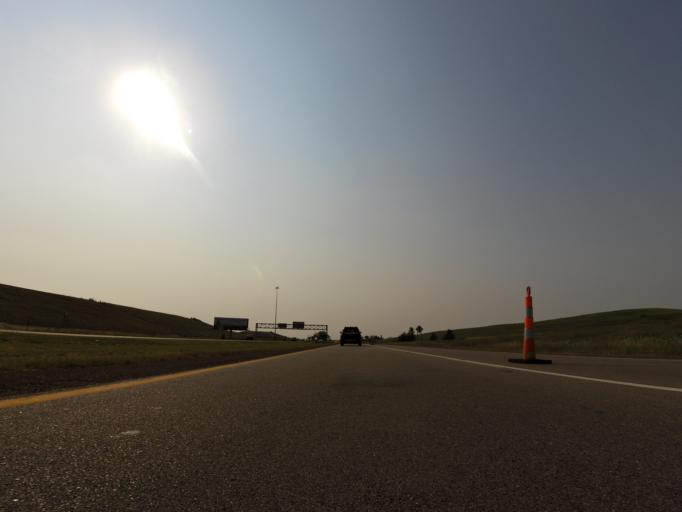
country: US
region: Kansas
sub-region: Sedgwick County
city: Maize
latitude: 37.7568
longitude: -97.3909
